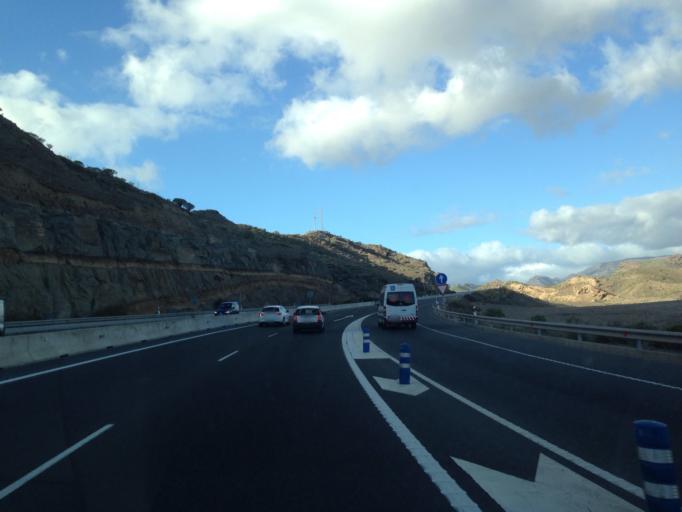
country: ES
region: Canary Islands
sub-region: Provincia de Las Palmas
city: Puerto Rico
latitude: 27.7675
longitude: -15.6745
